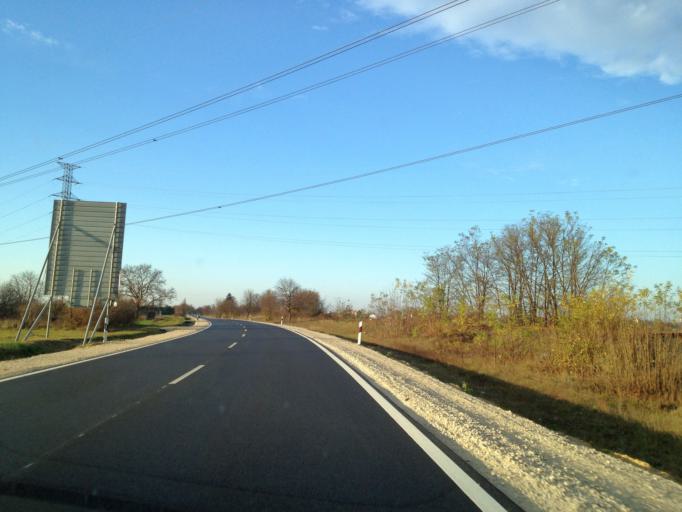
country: HU
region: Gyor-Moson-Sopron
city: Gyorujbarat
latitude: 47.6364
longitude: 17.6691
